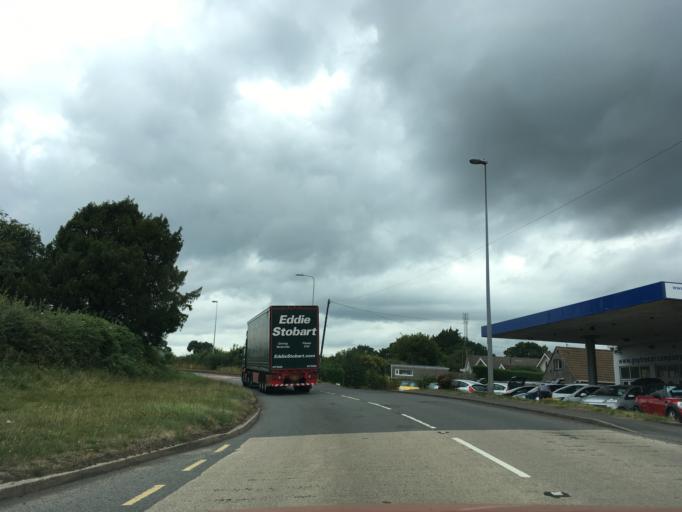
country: GB
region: Wales
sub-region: Torfaen County Borough
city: New Inn
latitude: 51.7370
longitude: -2.9827
